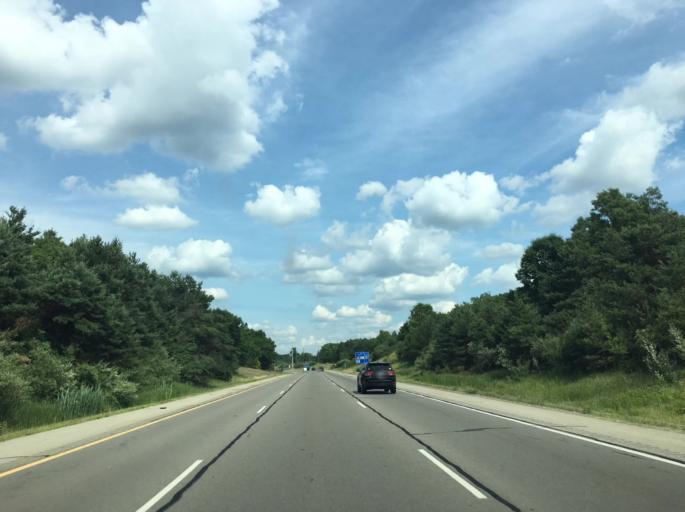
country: US
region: Michigan
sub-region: Oakland County
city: Clarkston
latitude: 42.7379
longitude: -83.4617
